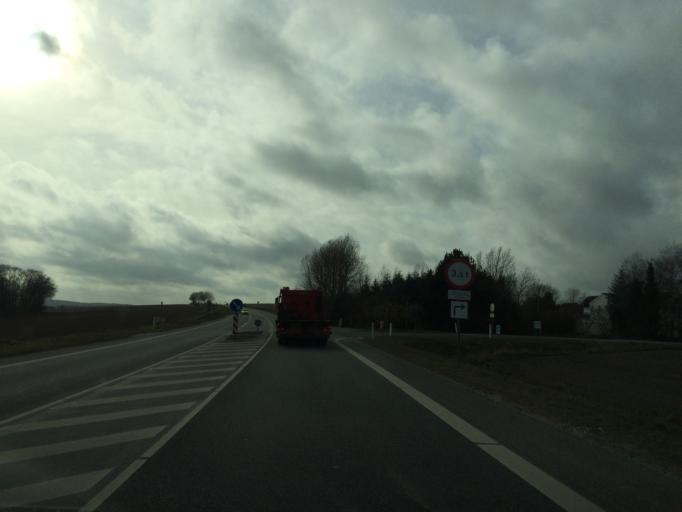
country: DK
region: Central Jutland
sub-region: Randers Kommune
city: Langa
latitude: 56.4798
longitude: 9.8950
